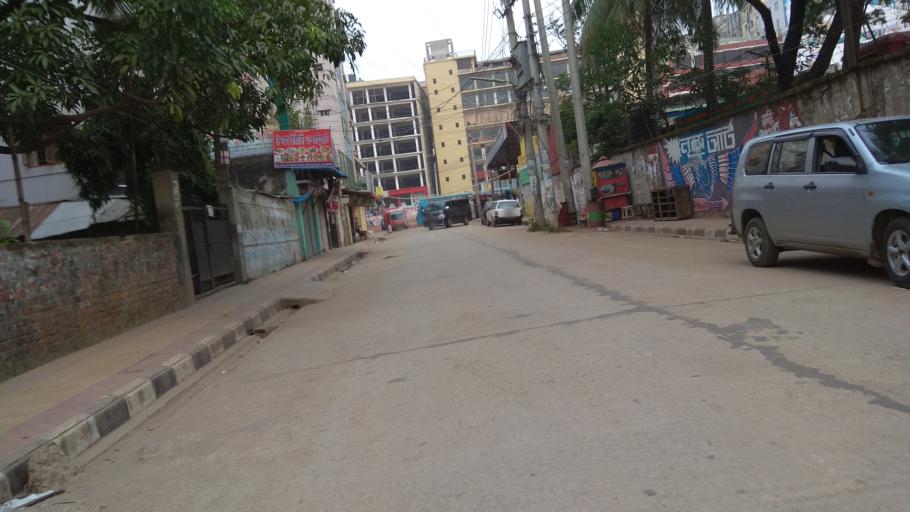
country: BD
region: Dhaka
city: Tungi
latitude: 23.8284
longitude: 90.3650
